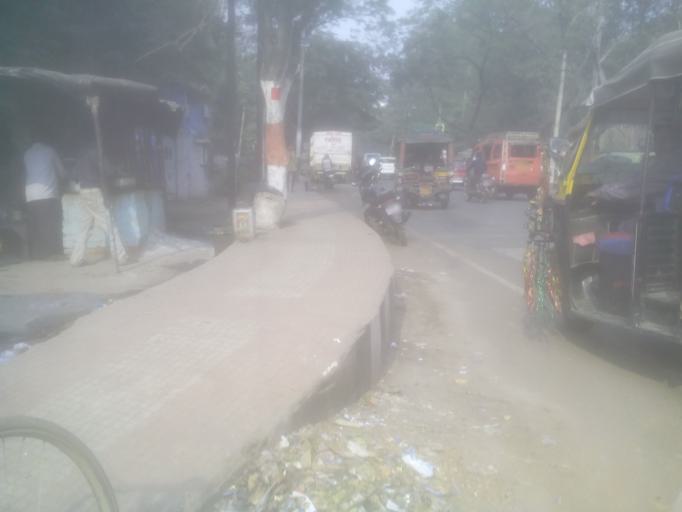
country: IN
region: Jharkhand
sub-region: Dhanbad
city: Dhanbad
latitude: 23.8018
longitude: 86.4268
